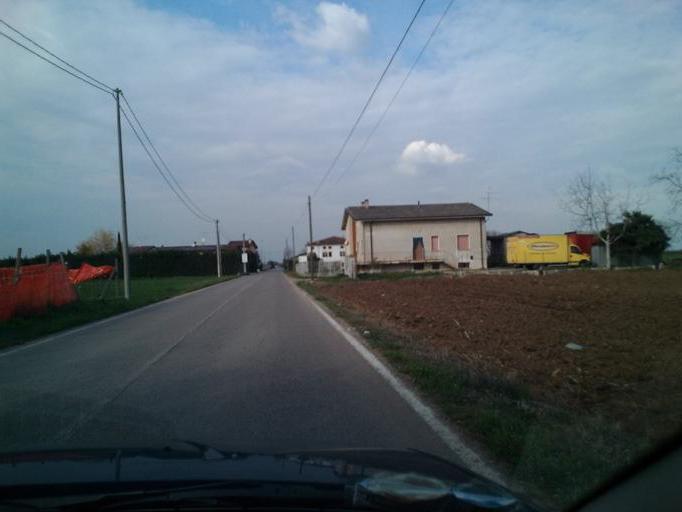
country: IT
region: Veneto
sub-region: Provincia di Verona
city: Villafranca di Verona
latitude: 45.3750
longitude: 10.8632
